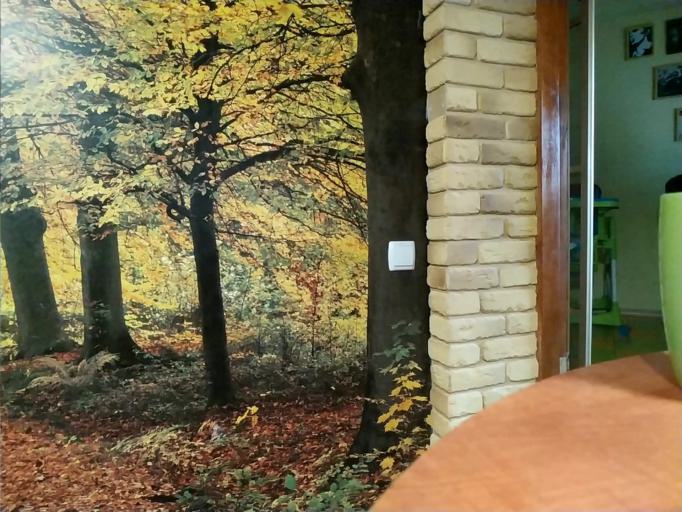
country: RU
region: Tverskaya
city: Staraya Toropa
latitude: 56.3507
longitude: 31.8148
